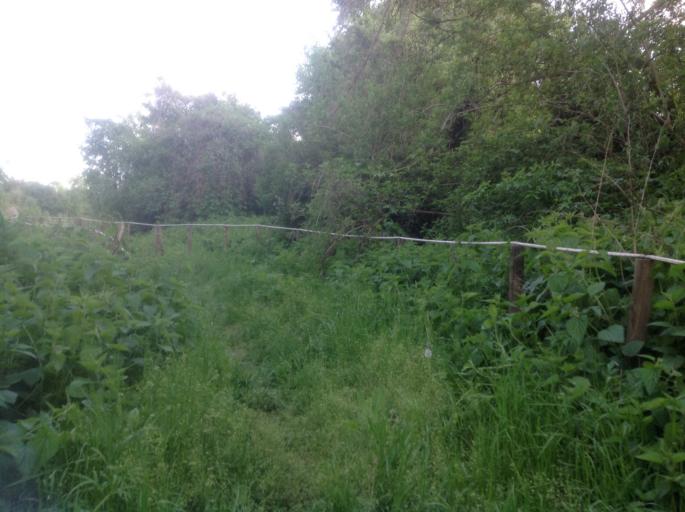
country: IT
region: Latium
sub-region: Provincia di Rieti
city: Colli sul Velino
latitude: 42.4722
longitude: 12.8055
